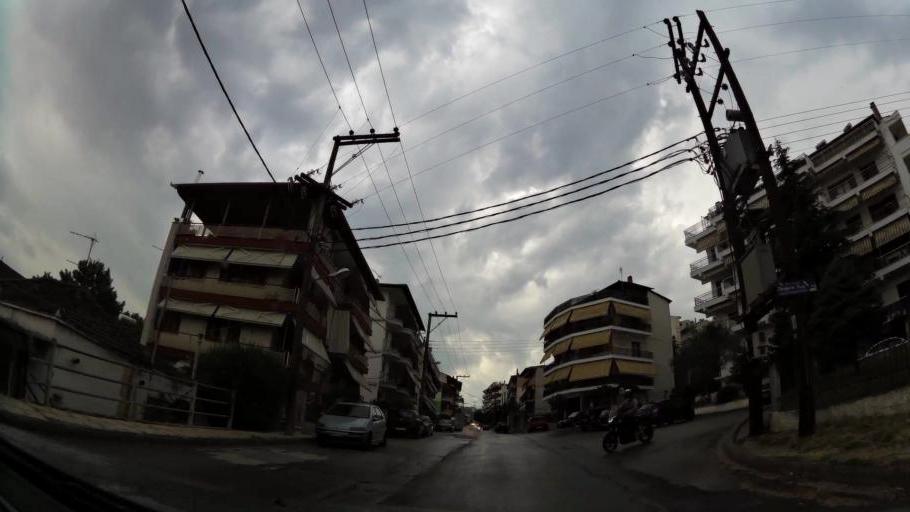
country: GR
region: Central Macedonia
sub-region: Nomos Imathias
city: Veroia
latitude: 40.5225
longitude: 22.1958
